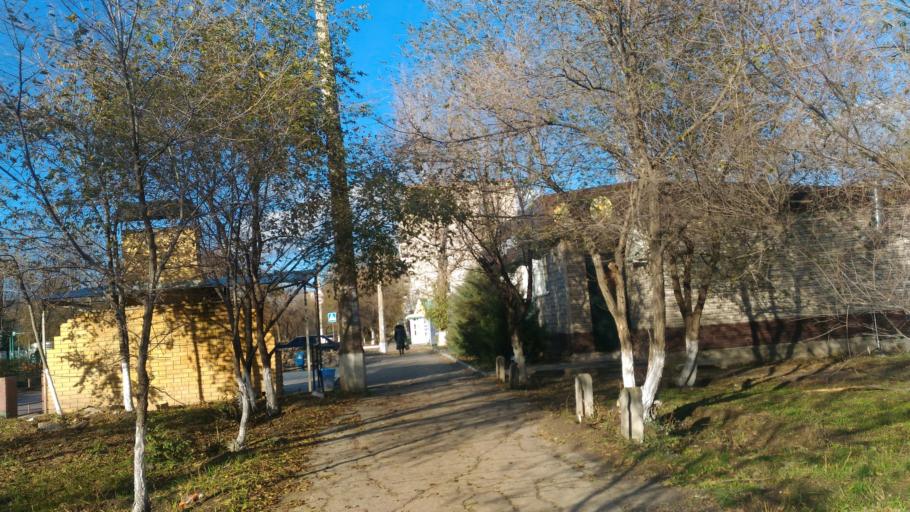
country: RU
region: Volgograd
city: Volgograd
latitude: 48.6064
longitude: 44.4228
